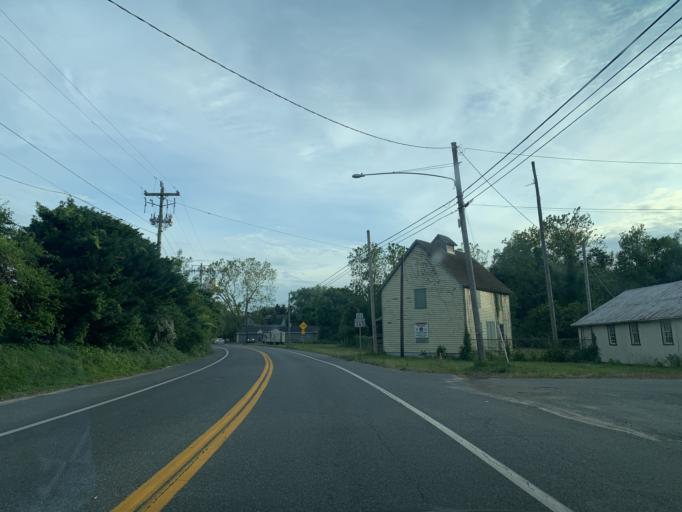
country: US
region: Maryland
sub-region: Worcester County
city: Snow Hill
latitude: 38.1797
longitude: -75.3893
